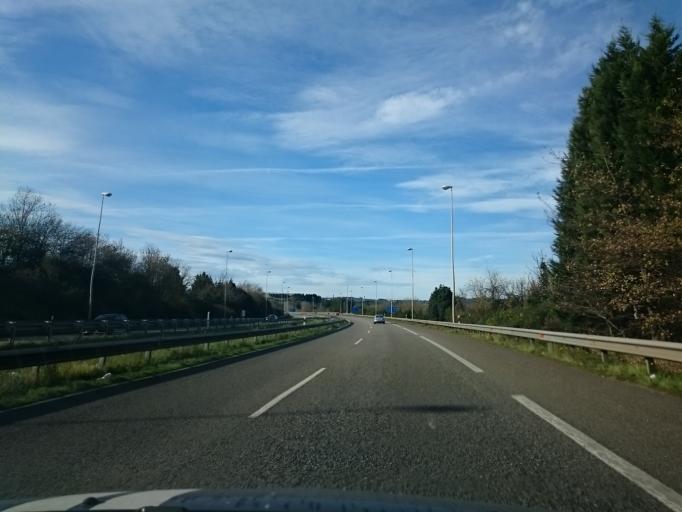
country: ES
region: Asturias
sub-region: Province of Asturias
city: Natahoyo
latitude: 43.5183
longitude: -5.6946
